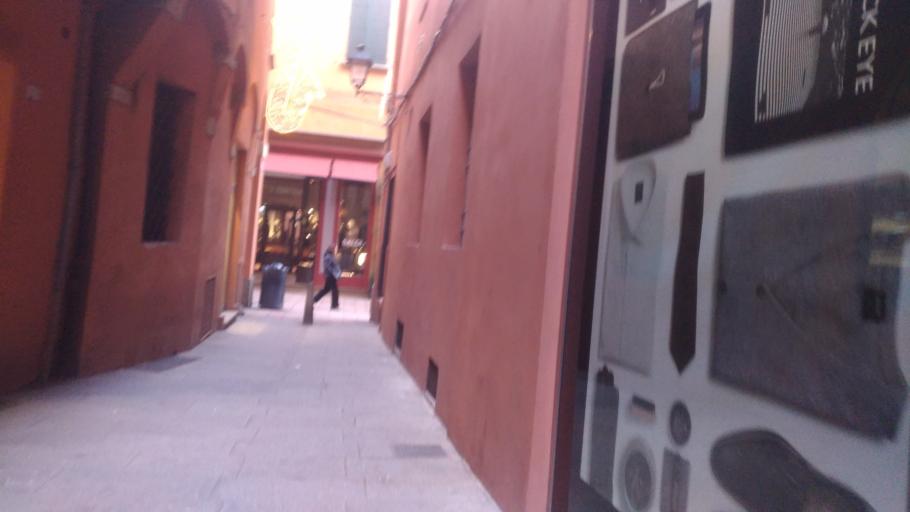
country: IT
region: Emilia-Romagna
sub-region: Provincia di Bologna
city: Bologna
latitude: 44.4925
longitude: 11.3423
